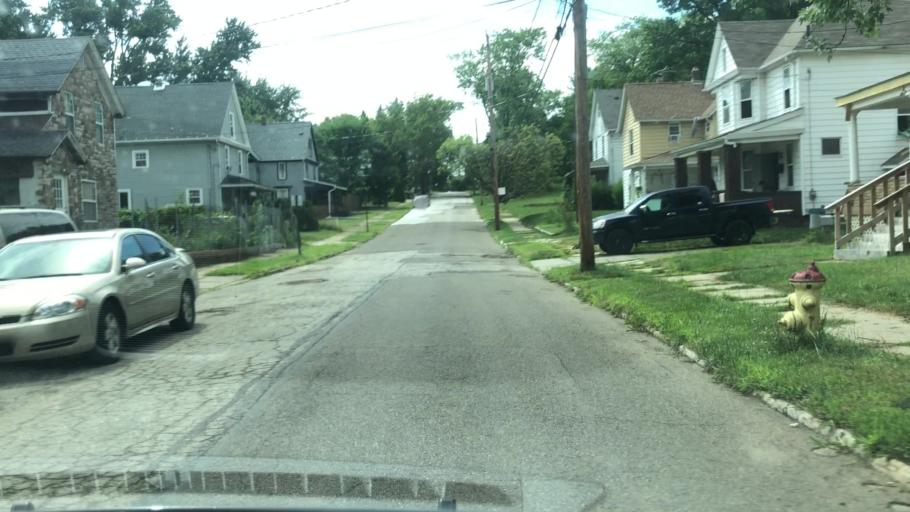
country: US
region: Ohio
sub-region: Summit County
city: Akron
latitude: 41.0603
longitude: -81.5298
